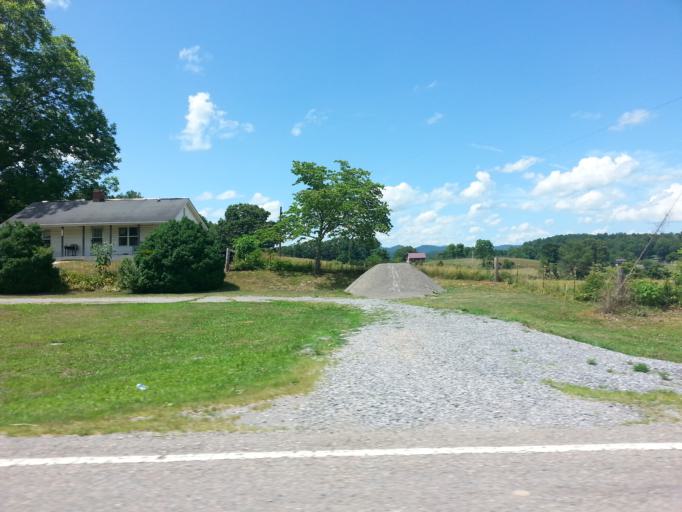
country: US
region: Virginia
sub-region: Lee County
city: Jonesville
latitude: 36.6956
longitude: -83.0503
